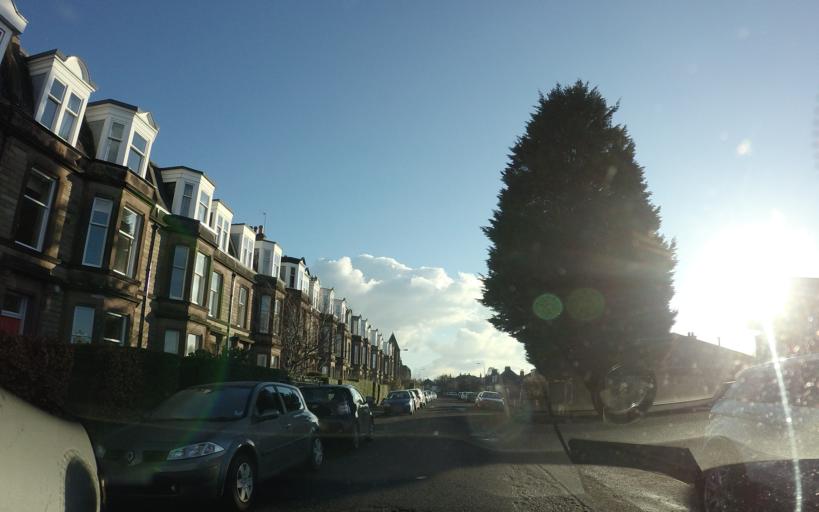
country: GB
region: Scotland
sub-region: Edinburgh
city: Edinburgh
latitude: 55.9765
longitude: -3.2115
